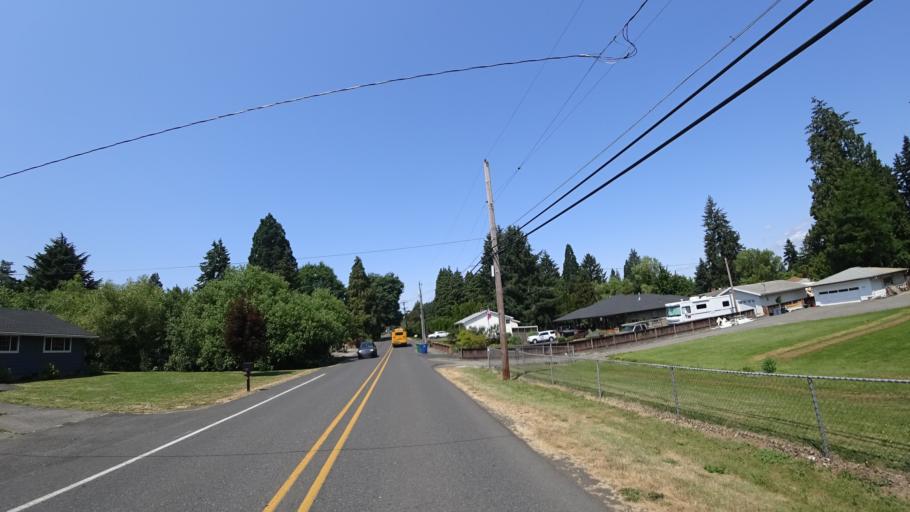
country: US
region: Oregon
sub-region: Clackamas County
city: Oatfield
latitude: 45.4446
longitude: -122.5924
